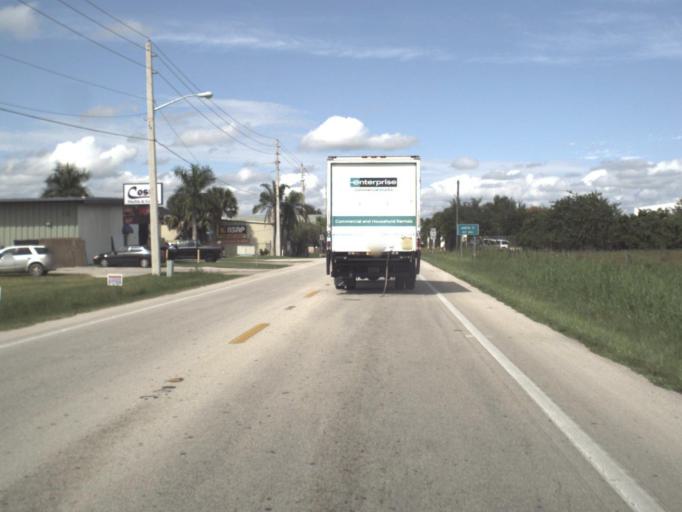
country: US
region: Florida
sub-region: Lee County
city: Fort Myers
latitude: 26.6200
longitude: -81.8519
